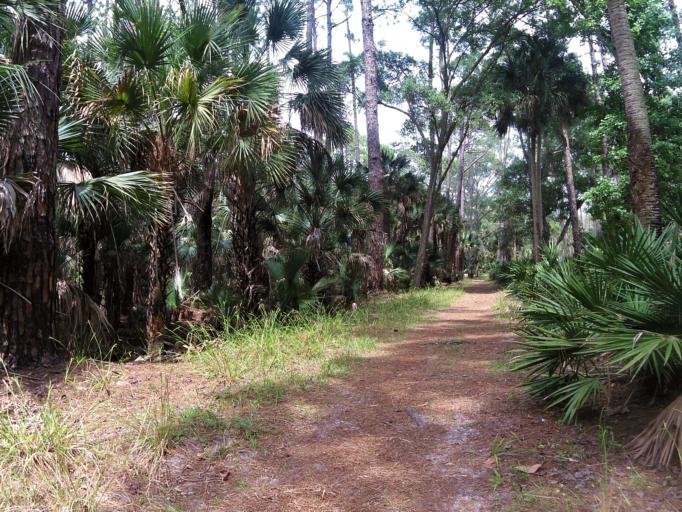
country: US
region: Florida
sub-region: Flagler County
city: Flagler Beach
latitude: 29.3985
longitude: -81.1270
